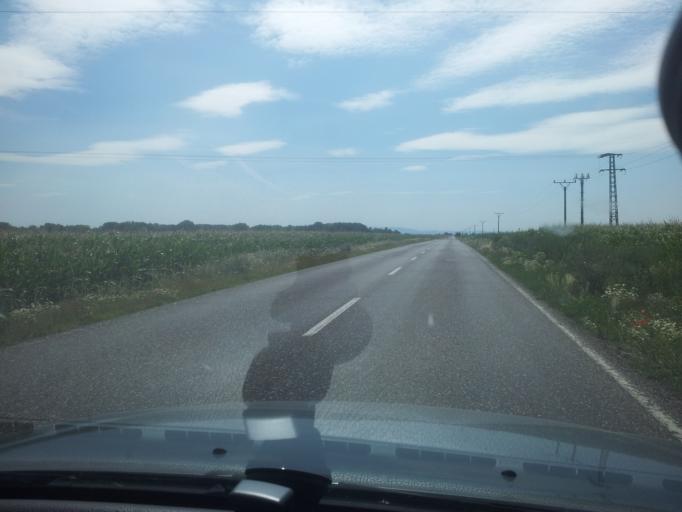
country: SK
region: Nitriansky
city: Levice
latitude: 48.1834
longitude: 18.5224
